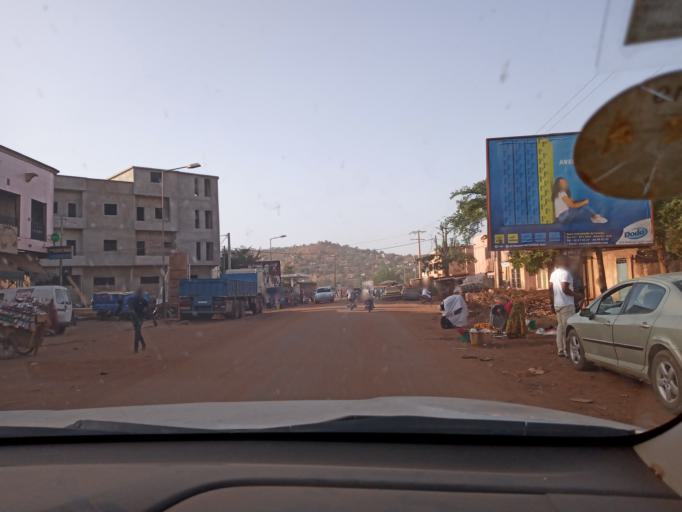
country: ML
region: Bamako
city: Bamako
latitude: 12.6700
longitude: -7.9776
